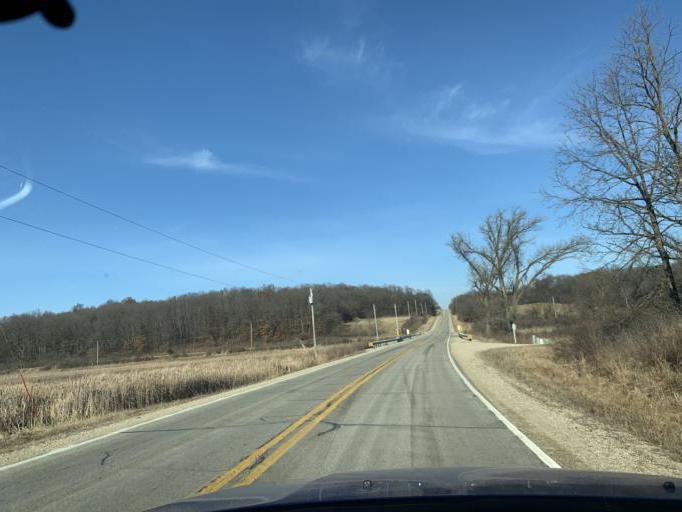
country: US
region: Wisconsin
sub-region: Green County
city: New Glarus
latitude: 42.7369
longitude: -89.8610
